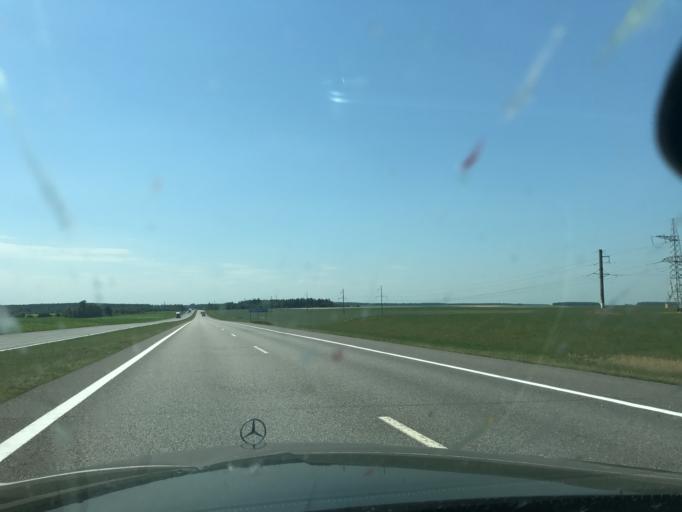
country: BY
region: Minsk
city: Haradzyeya
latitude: 53.3962
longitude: 26.5366
